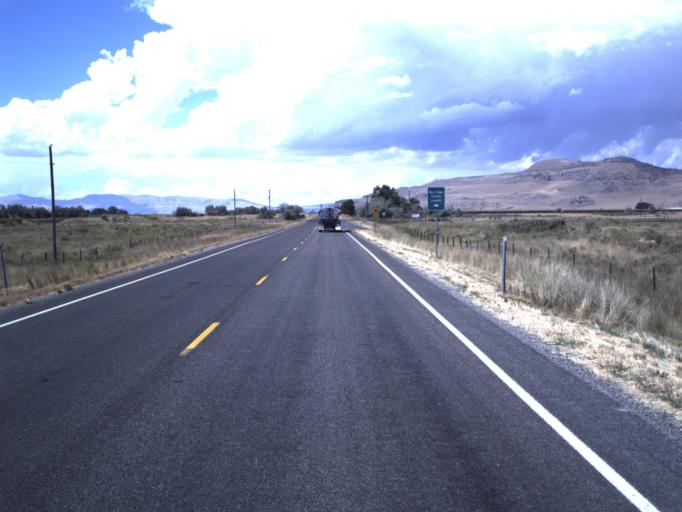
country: US
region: Utah
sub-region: Box Elder County
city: Honeyville
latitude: 41.5645
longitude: -112.1743
